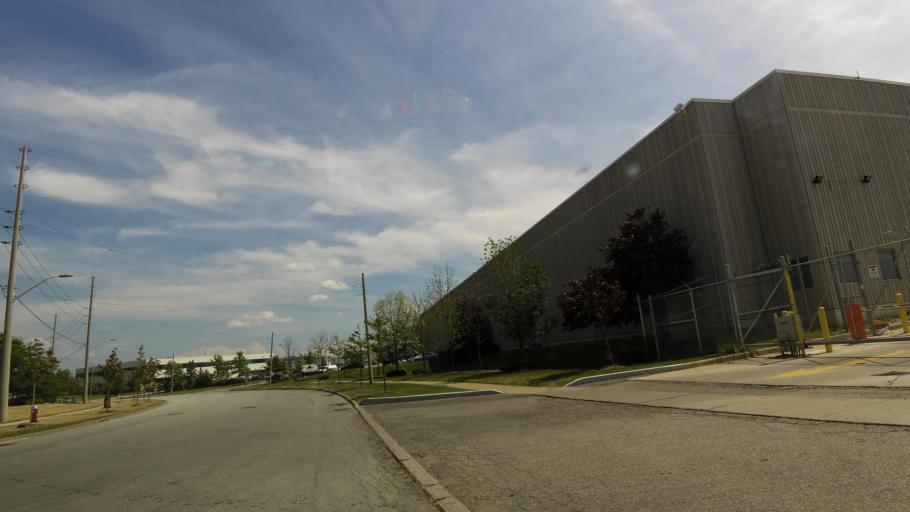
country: CA
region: Ontario
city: Etobicoke
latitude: 43.6490
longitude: -79.6249
